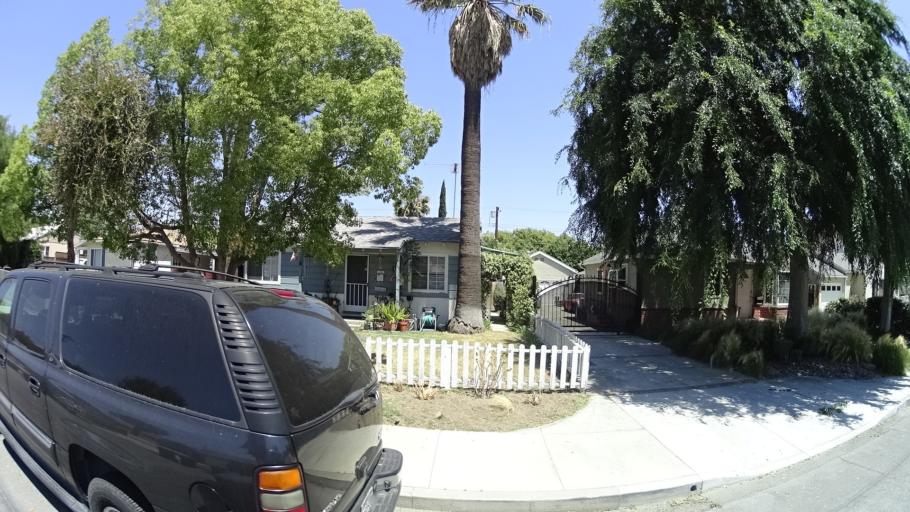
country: US
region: California
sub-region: Los Angeles County
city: Burbank
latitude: 34.1838
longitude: -118.3448
